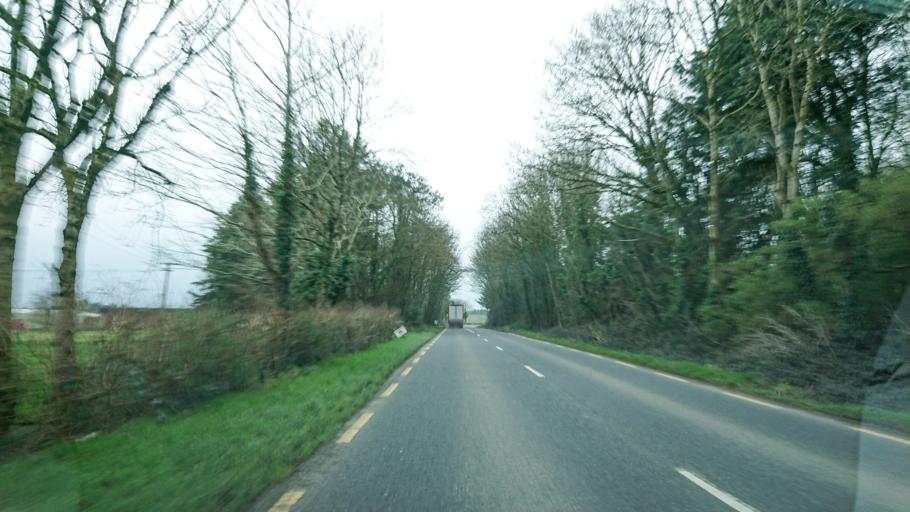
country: IE
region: Munster
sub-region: County Cork
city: Bandon
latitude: 51.7461
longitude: -8.7924
